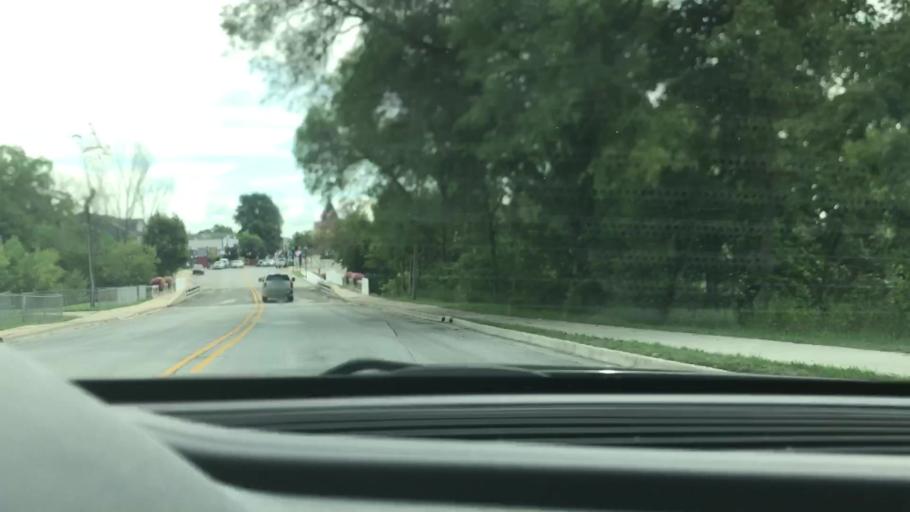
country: US
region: Michigan
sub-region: Antrim County
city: Bellaire
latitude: 44.9793
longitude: -85.2103
